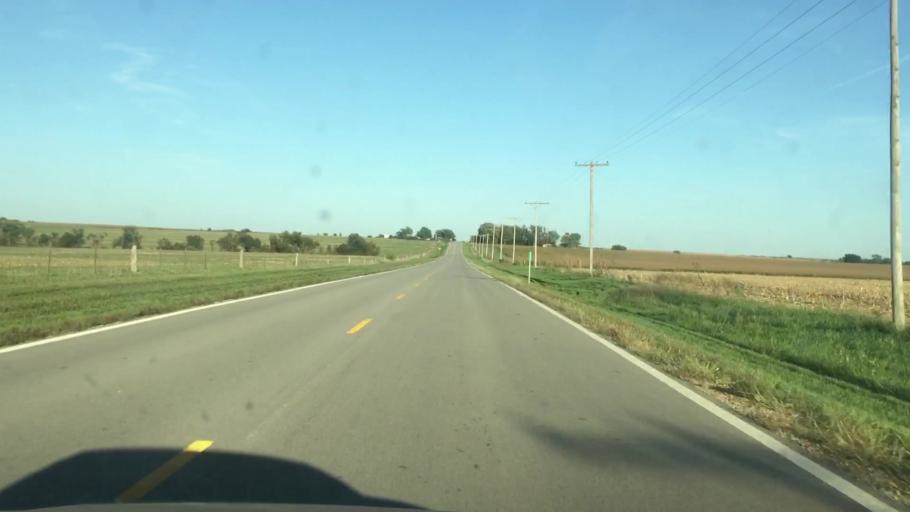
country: US
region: Kansas
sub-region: Brown County
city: Horton
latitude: 39.5876
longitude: -95.6003
